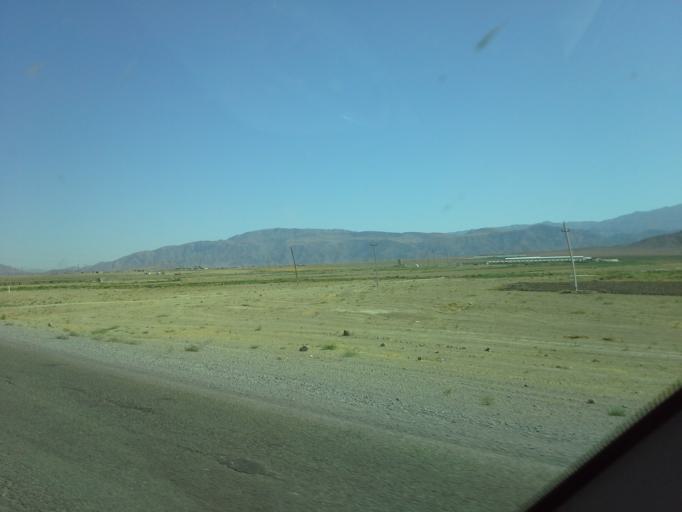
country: TM
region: Ahal
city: Baharly
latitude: 38.4538
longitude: 57.3670
